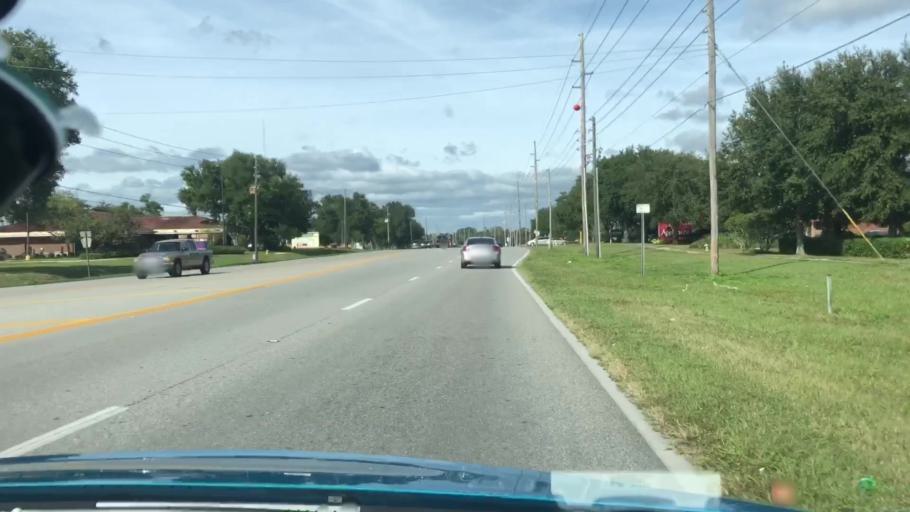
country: US
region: Florida
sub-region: Volusia County
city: Deltona
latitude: 28.9136
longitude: -81.2931
